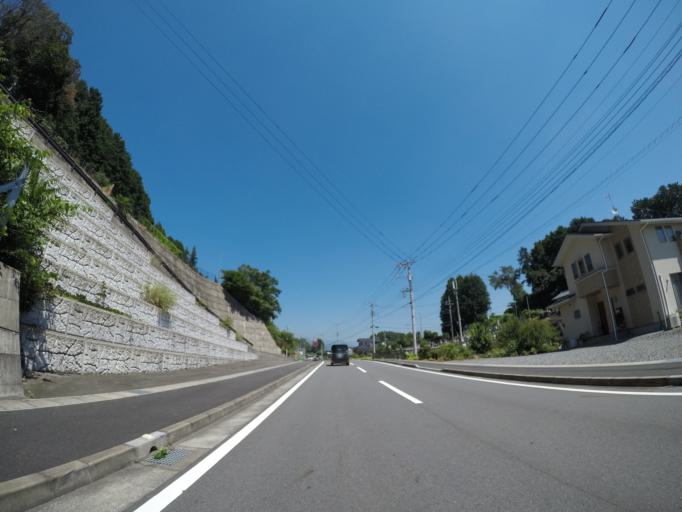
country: JP
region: Shizuoka
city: Fujinomiya
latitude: 35.2069
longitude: 138.5657
